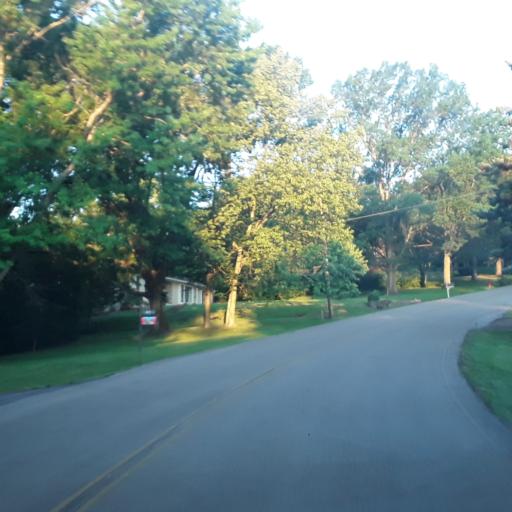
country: US
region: Tennessee
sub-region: Davidson County
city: Oak Hill
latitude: 36.0678
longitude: -86.7768
